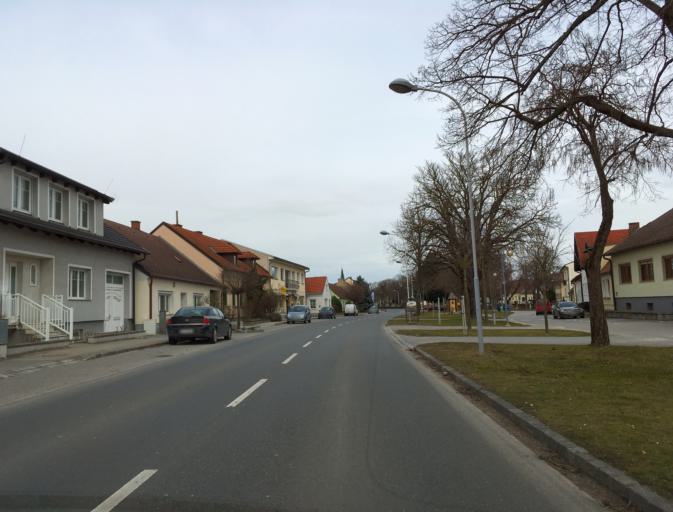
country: AT
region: Lower Austria
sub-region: Politischer Bezirk Ganserndorf
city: Lassee
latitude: 48.2211
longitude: 16.8164
